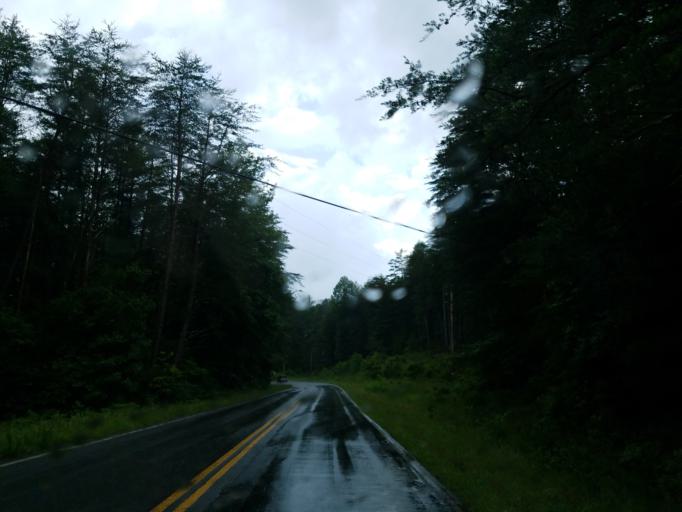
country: US
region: Georgia
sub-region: Fannin County
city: Blue Ridge
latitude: 34.7678
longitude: -84.2573
